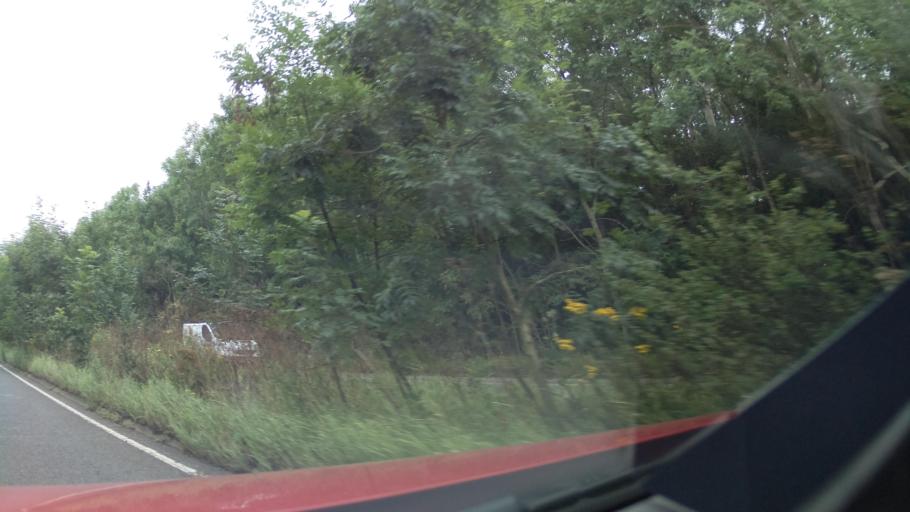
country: GB
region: England
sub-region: Northamptonshire
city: Geddington
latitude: 52.4557
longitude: -0.7366
